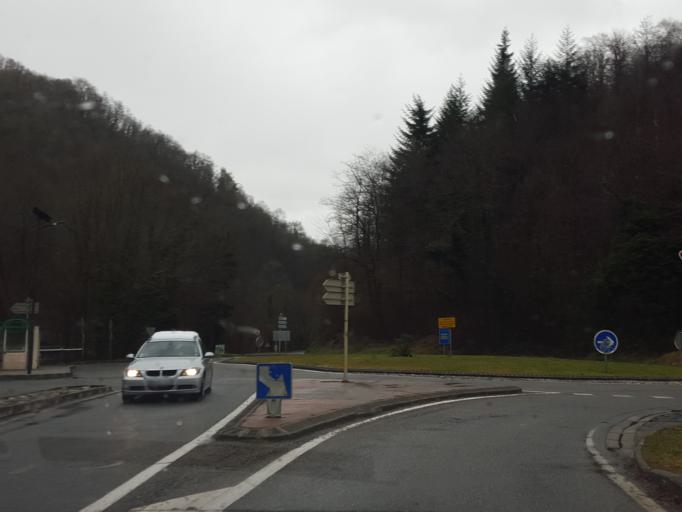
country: FR
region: Midi-Pyrenees
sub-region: Departement de l'Ariege
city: Saint-Girons
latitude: 42.9093
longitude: 1.2141
